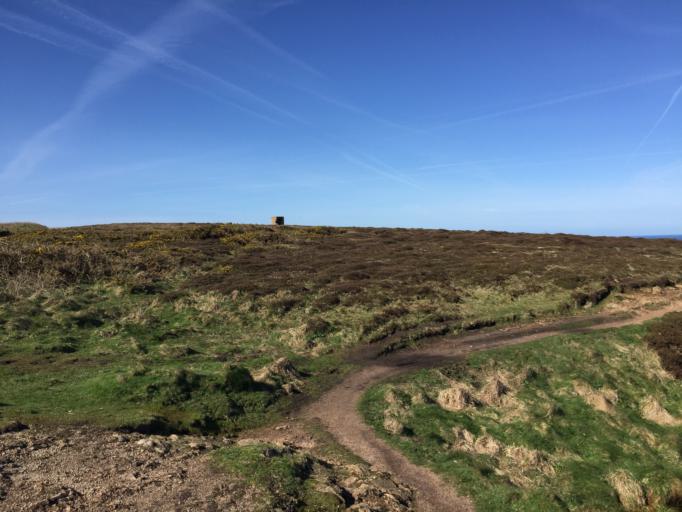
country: JE
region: St Helier
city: Saint Helier
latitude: 49.2555
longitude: -2.2465
